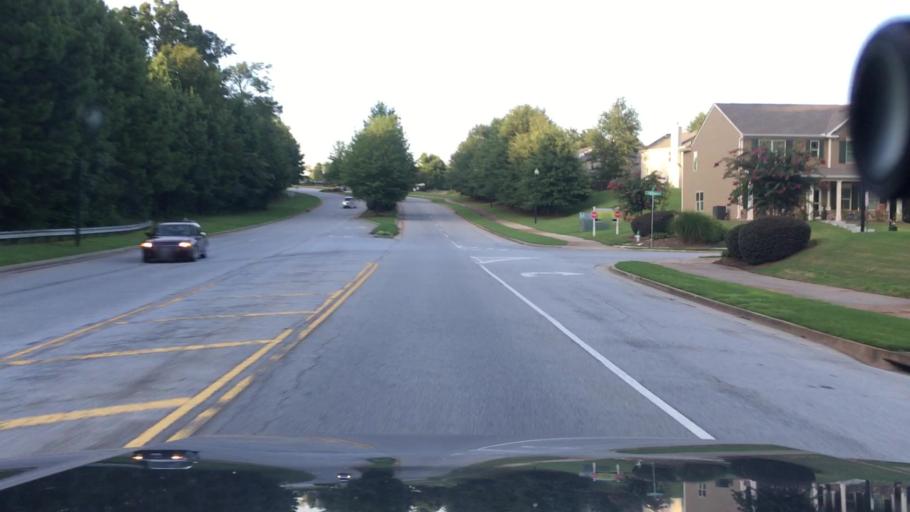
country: US
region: Georgia
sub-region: Coweta County
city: East Newnan
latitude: 33.3711
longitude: -84.7555
